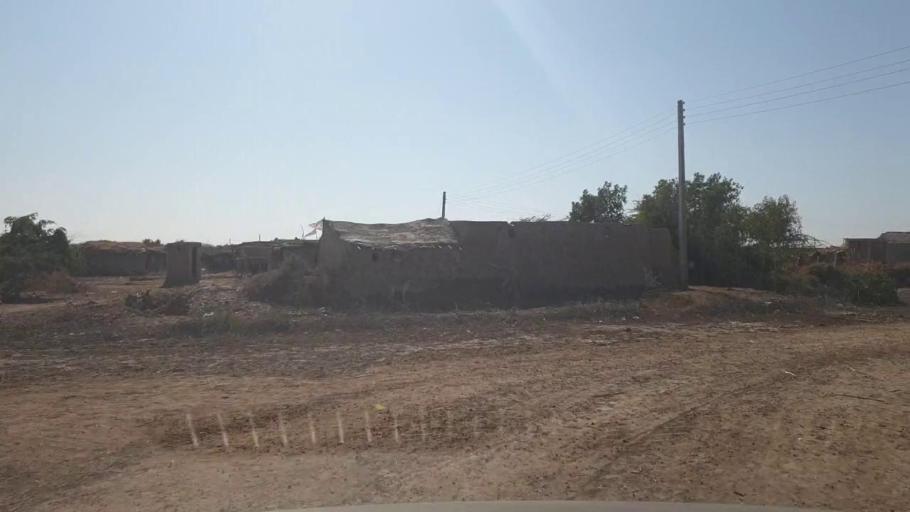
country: PK
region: Sindh
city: Dhoro Naro
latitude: 25.4089
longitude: 69.5895
